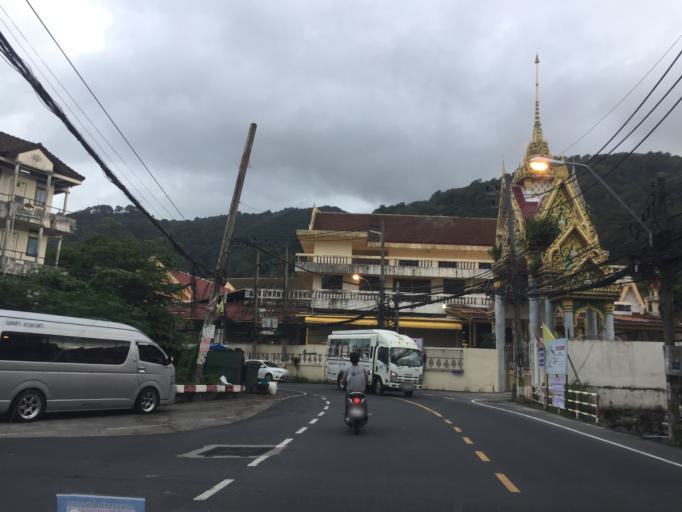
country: TH
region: Phuket
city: Patong
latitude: 7.9014
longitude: 98.3105
